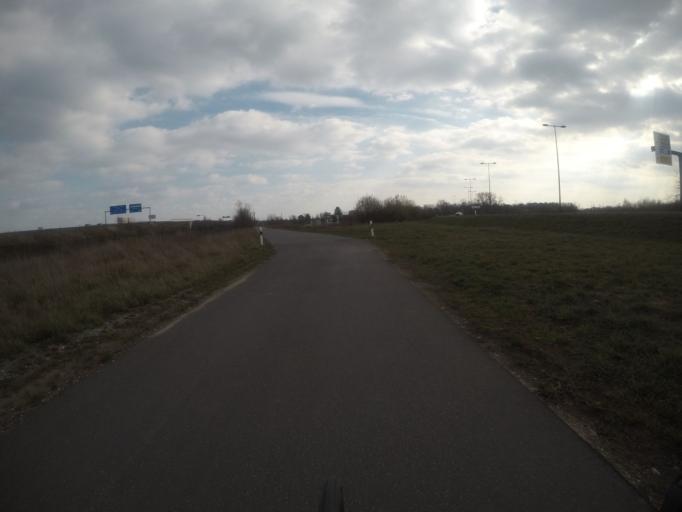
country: DE
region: Brandenburg
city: Schonefeld
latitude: 52.3800
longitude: 13.5399
